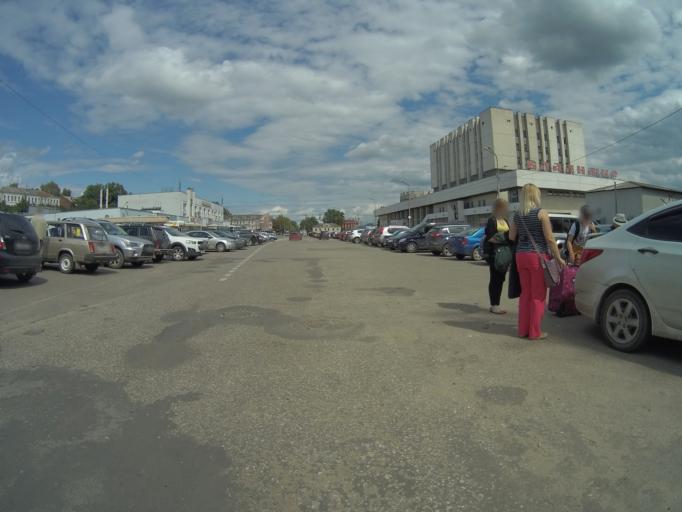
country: RU
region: Vladimir
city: Vladimir
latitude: 56.1297
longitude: 40.4180
